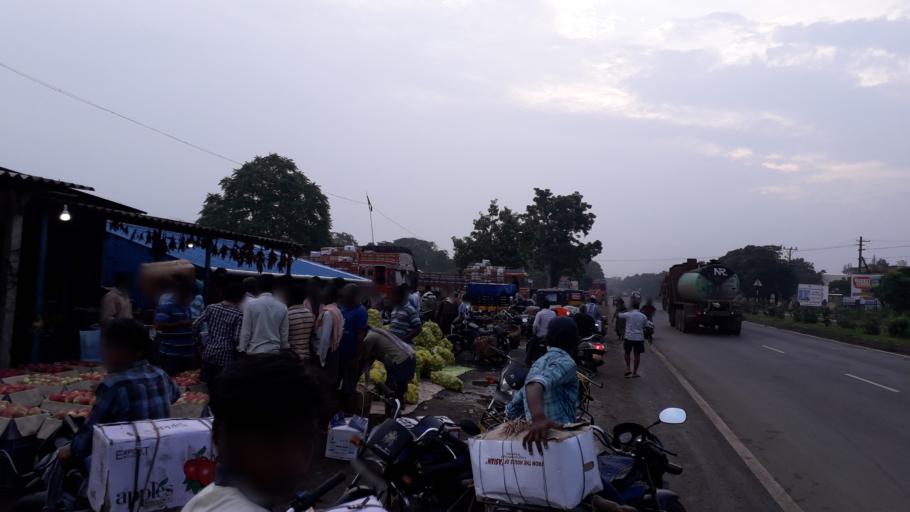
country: IN
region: Andhra Pradesh
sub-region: East Godavari
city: Rajahmundry
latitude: 17.0478
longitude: 81.8495
